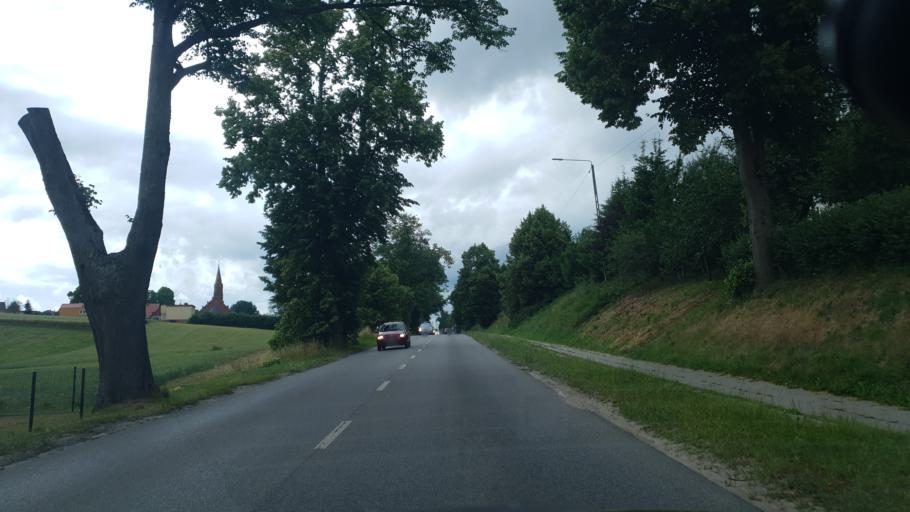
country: PL
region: Pomeranian Voivodeship
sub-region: Powiat kartuski
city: Przodkowo
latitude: 54.3782
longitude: 18.2947
